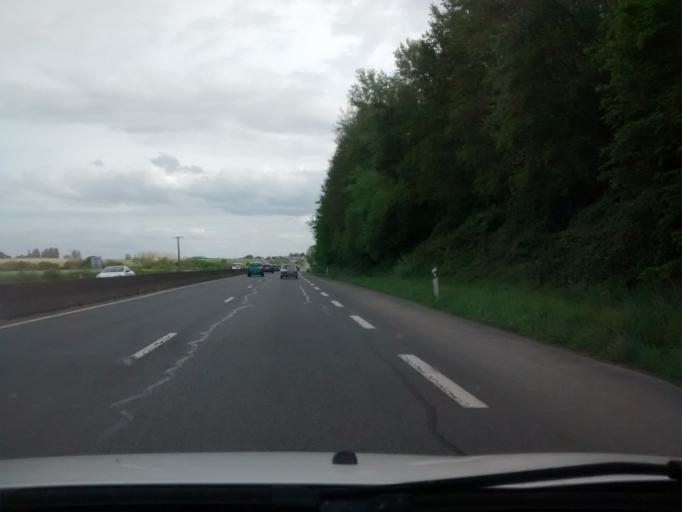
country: FR
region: Brittany
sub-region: Departement d'Ille-et-Vilaine
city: Saint-Jouan-des-Guerets
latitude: 48.5990
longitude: -1.9671
